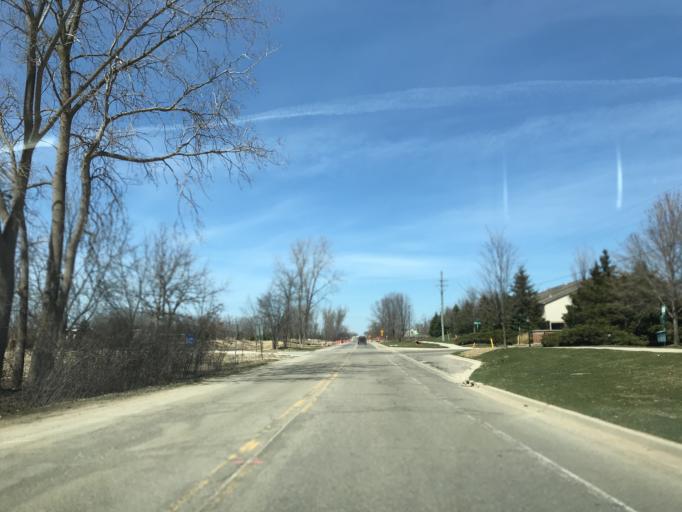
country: US
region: Michigan
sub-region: Washtenaw County
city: Ann Arbor
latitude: 42.3192
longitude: -83.7077
